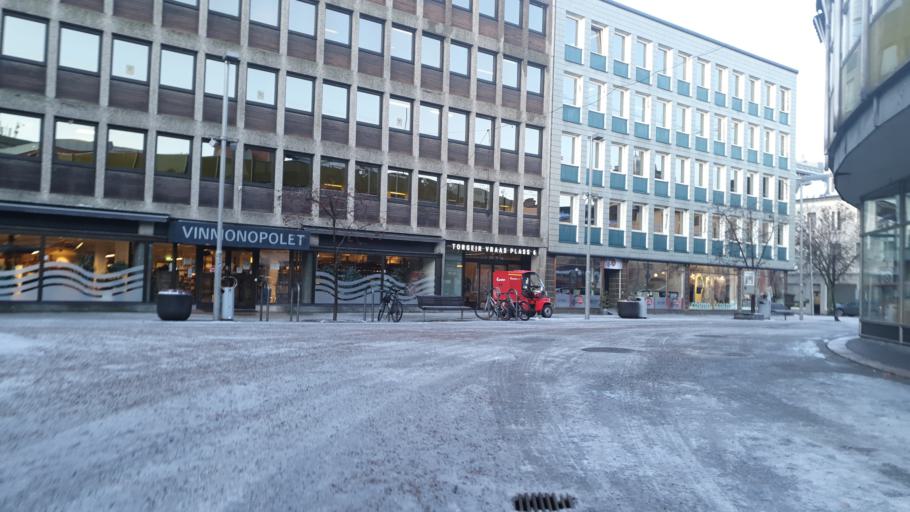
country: NO
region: Buskerud
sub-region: Drammen
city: Drammen
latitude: 59.7390
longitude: 10.2011
